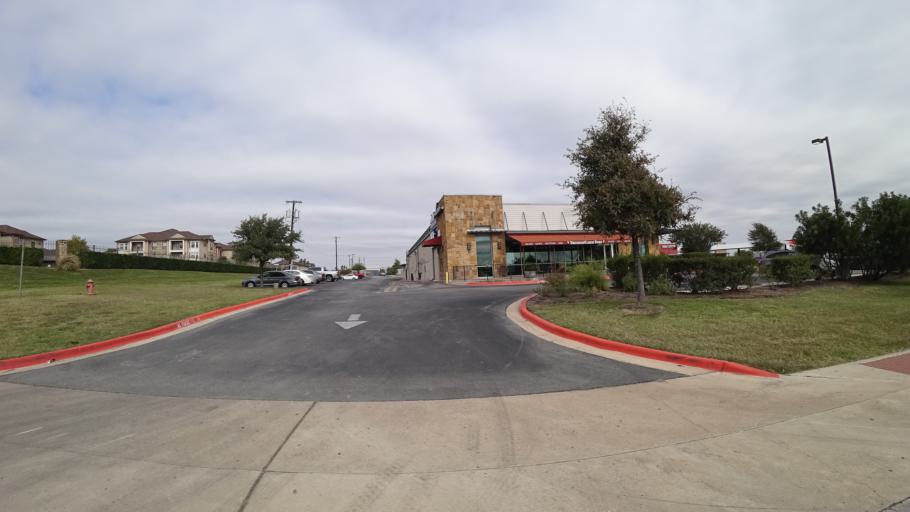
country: US
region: Texas
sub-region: Travis County
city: Windemere
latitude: 30.4559
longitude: -97.6614
